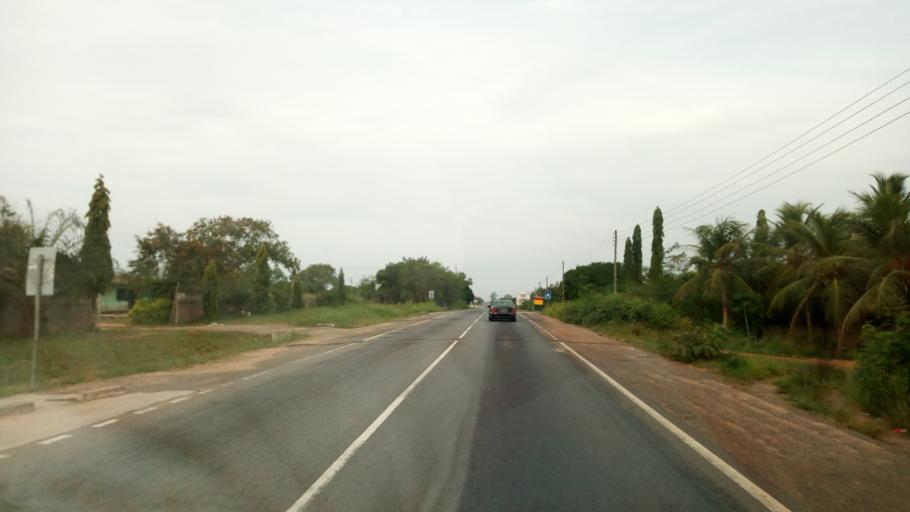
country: GH
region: Volta
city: Keta
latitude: 6.0662
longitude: 1.0130
